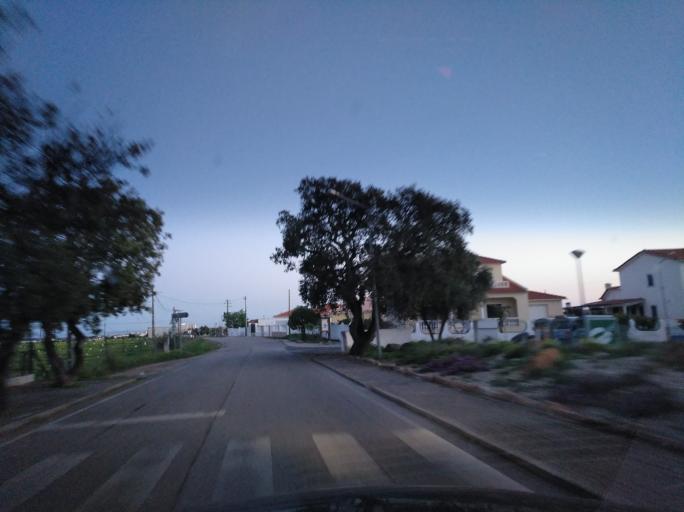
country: PT
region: Faro
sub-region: Vila Real de Santo Antonio
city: Monte Gordo
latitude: 37.1889
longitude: -7.5107
